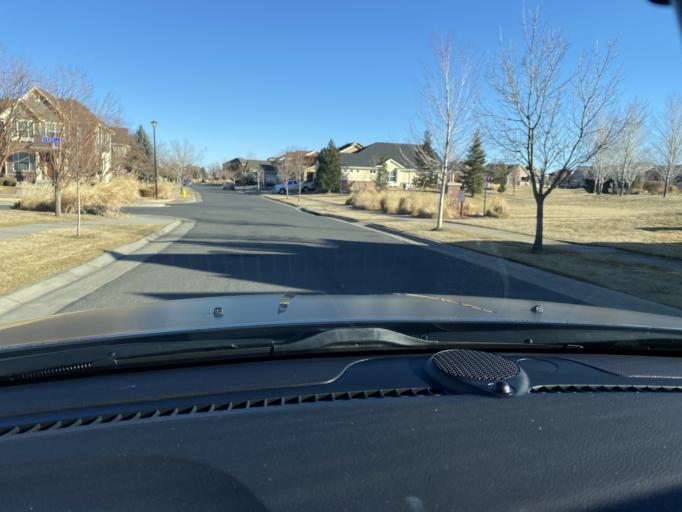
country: US
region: Colorado
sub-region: Jefferson County
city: Arvada
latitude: 39.8487
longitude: -105.1591
